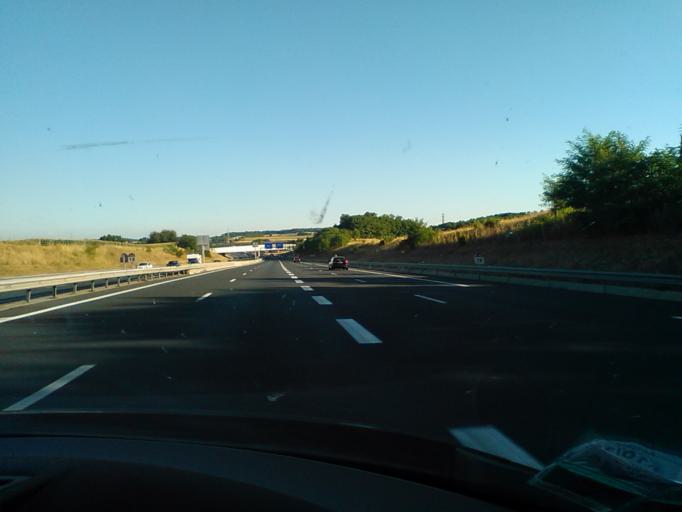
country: FR
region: Rhone-Alpes
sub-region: Departement du Rhone
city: Cailloux-sur-Fontaines
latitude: 45.8715
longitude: 4.9043
